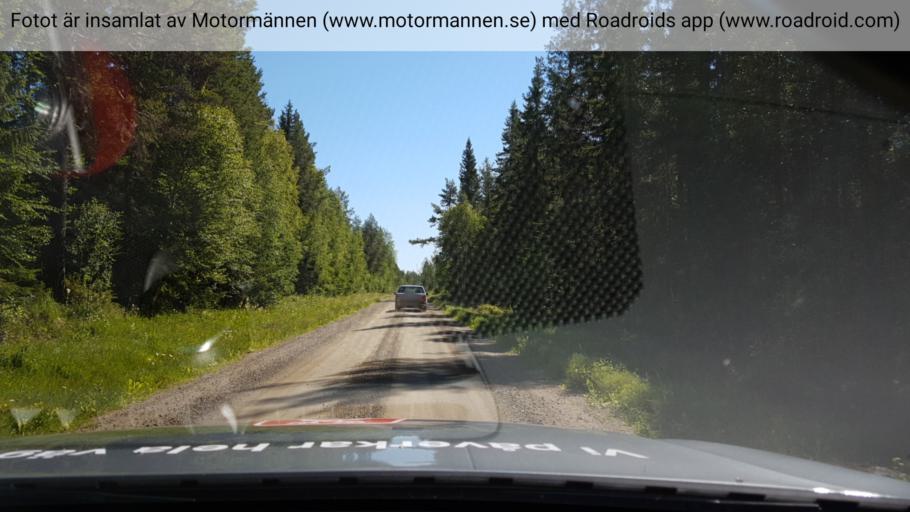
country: SE
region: Jaemtland
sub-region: Braecke Kommun
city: Braecke
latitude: 62.7989
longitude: 15.2507
